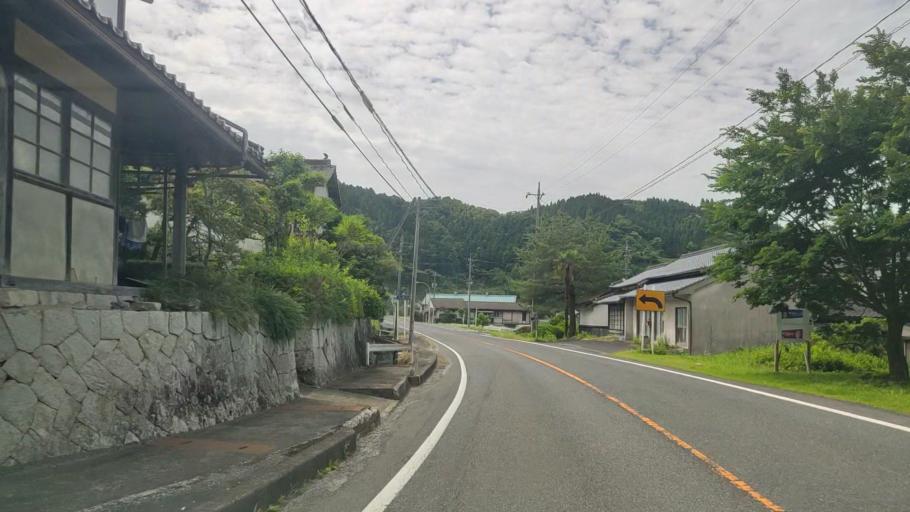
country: JP
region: Okayama
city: Niimi
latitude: 35.0948
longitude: 133.6528
